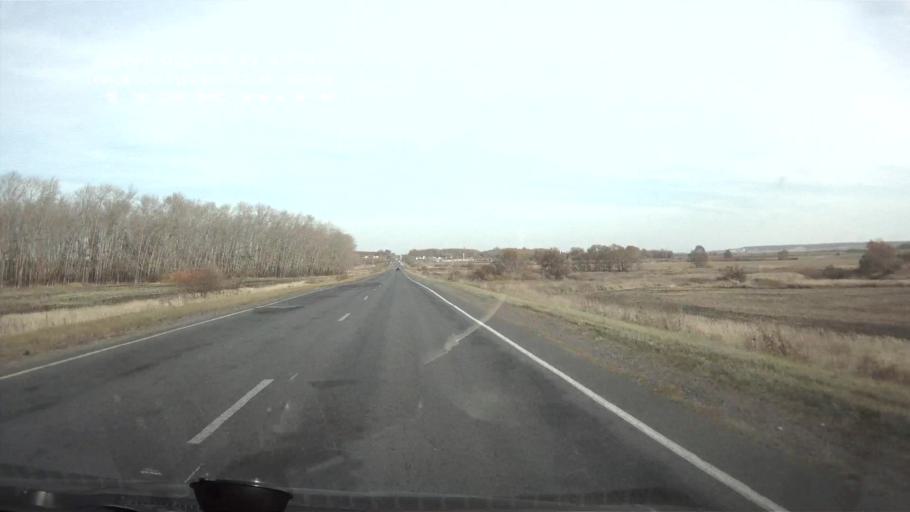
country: RU
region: Mordoviya
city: Atyashevo
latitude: 54.5522
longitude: 45.9591
